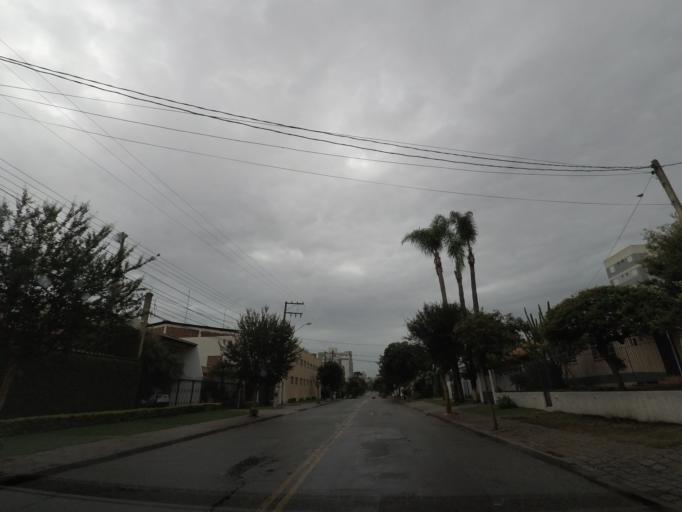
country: BR
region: Parana
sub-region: Curitiba
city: Curitiba
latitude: -25.4608
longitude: -49.2867
